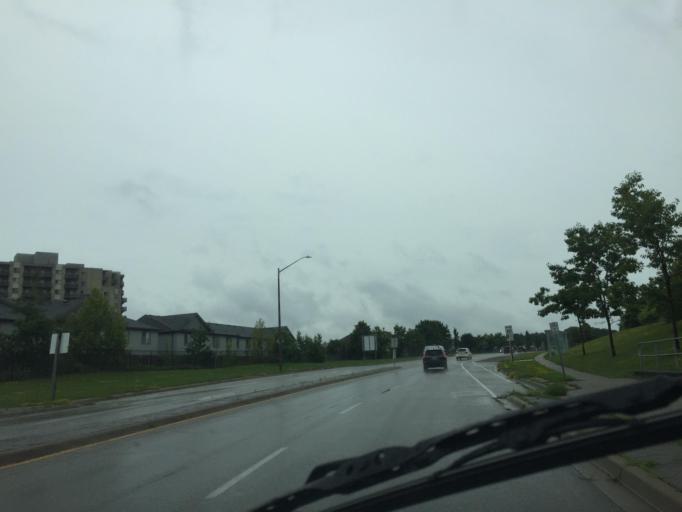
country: CA
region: Ontario
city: Cambridge
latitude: 43.3902
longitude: -80.3125
